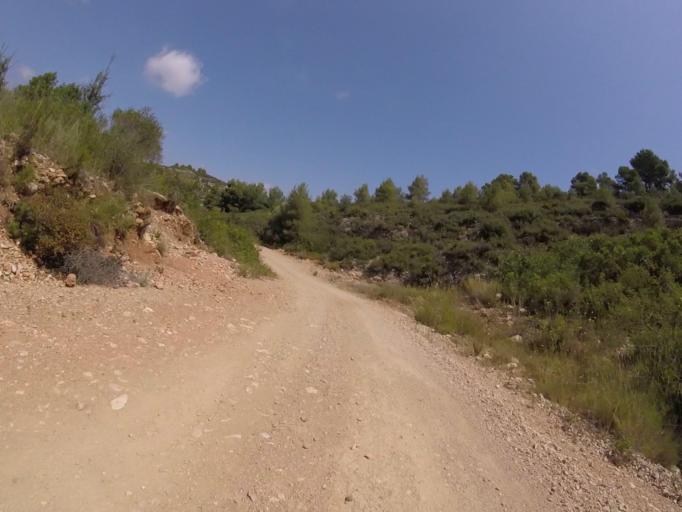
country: ES
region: Valencia
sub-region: Provincia de Castello
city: Torreblanca
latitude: 40.2193
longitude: 0.1489
